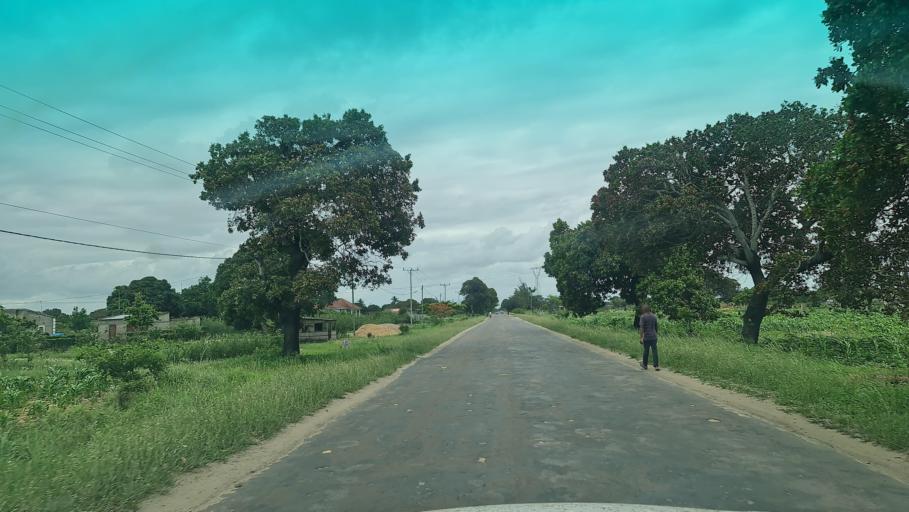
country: MZ
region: Maputo
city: Manhica
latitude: -25.4185
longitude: 32.7724
